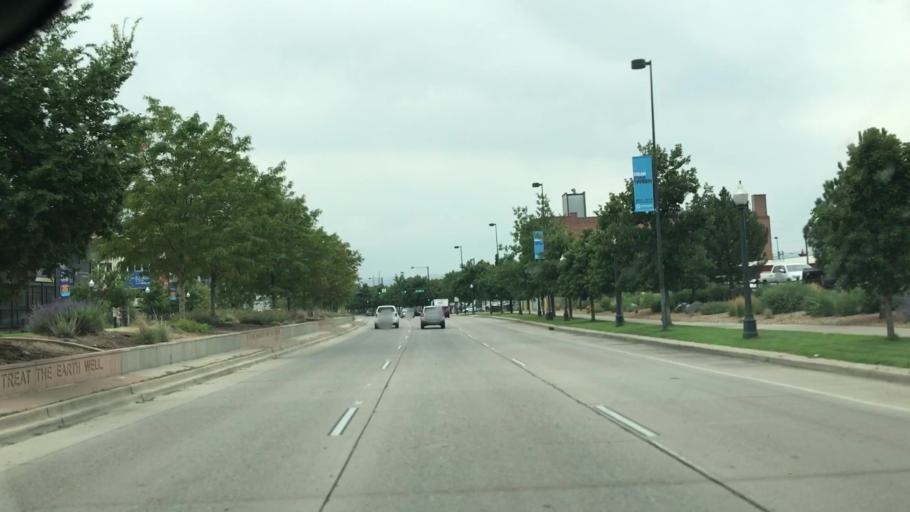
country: US
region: Colorado
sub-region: Denver County
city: Denver
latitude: 39.7474
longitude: -105.0059
